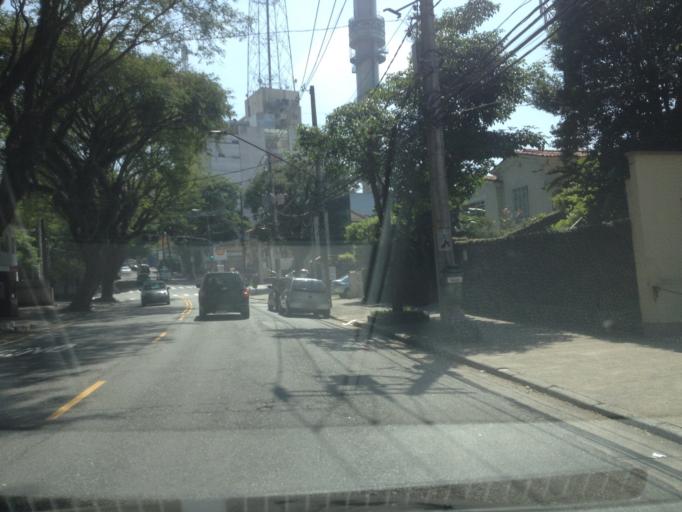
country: BR
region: Sao Paulo
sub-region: Sao Paulo
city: Sao Paulo
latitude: -23.5467
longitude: -46.6813
